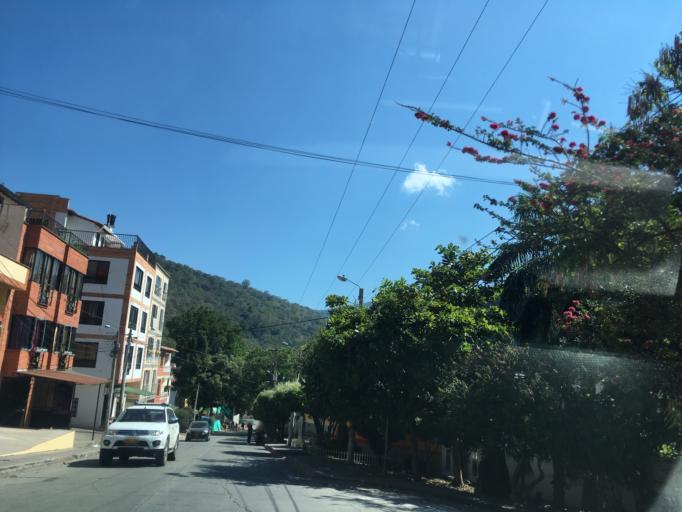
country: CO
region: Santander
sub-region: San Gil
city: San Gil
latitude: 6.5546
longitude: -73.1252
